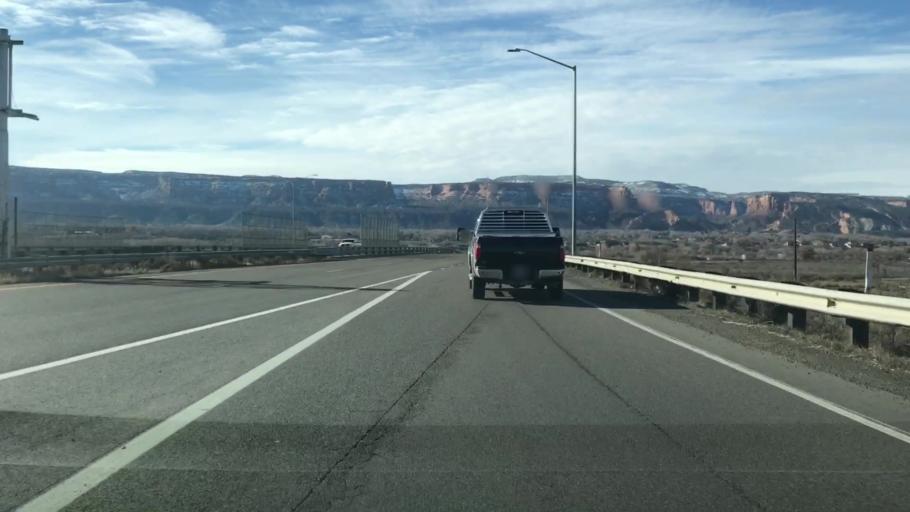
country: US
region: Colorado
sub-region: Mesa County
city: Redlands
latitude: 39.1113
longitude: -108.6469
